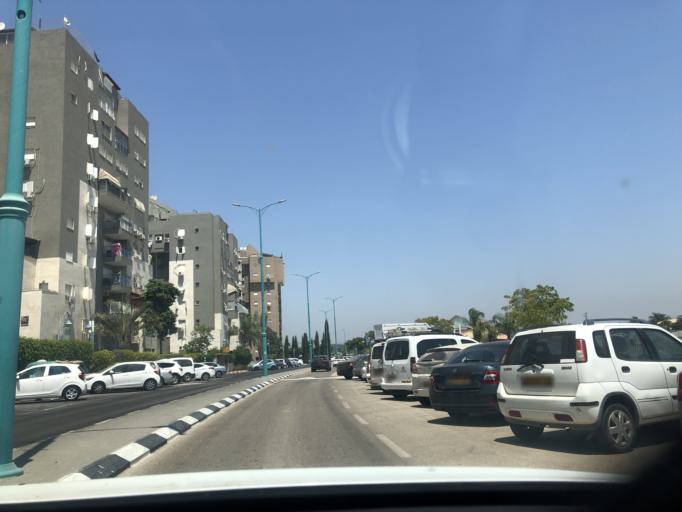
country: IL
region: Central District
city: Lod
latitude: 31.9444
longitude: 34.9043
